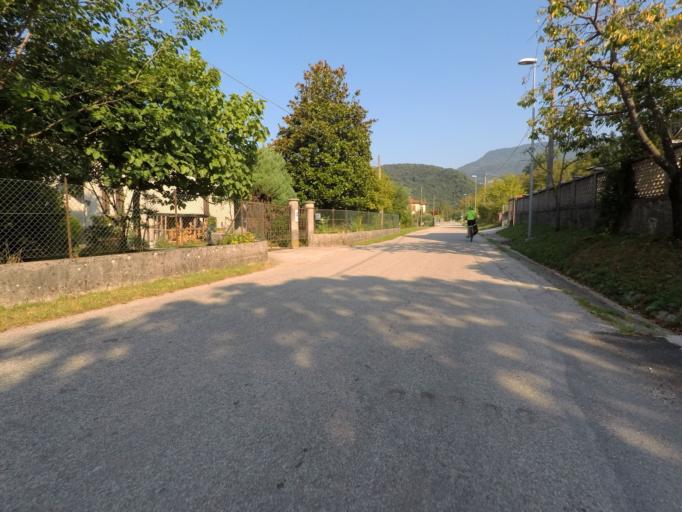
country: IT
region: Friuli Venezia Giulia
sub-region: Provincia di Udine
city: Forgaria nel Friuli
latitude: 46.2052
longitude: 12.9624
